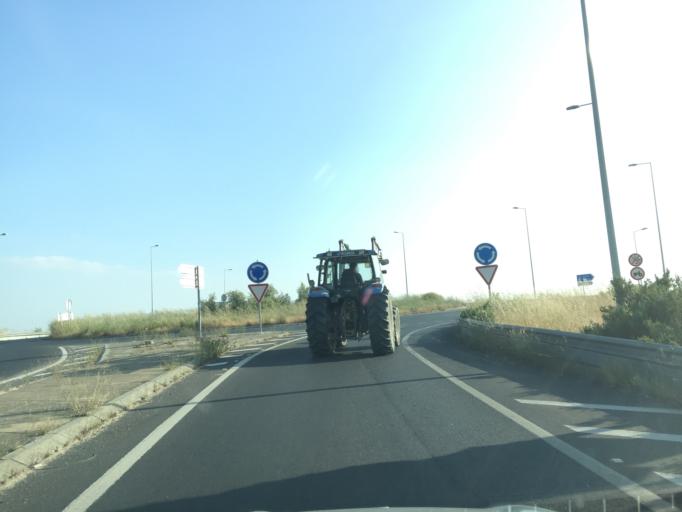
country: PT
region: Santarem
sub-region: Almeirim
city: Almeirim
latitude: 39.1914
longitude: -8.6475
